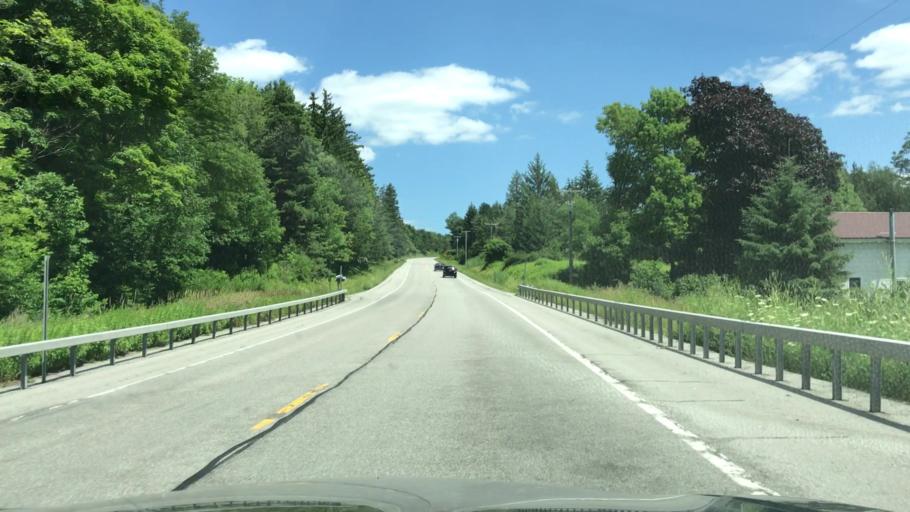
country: US
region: New York
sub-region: Wyoming County
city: Warsaw
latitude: 42.7491
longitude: -78.2429
